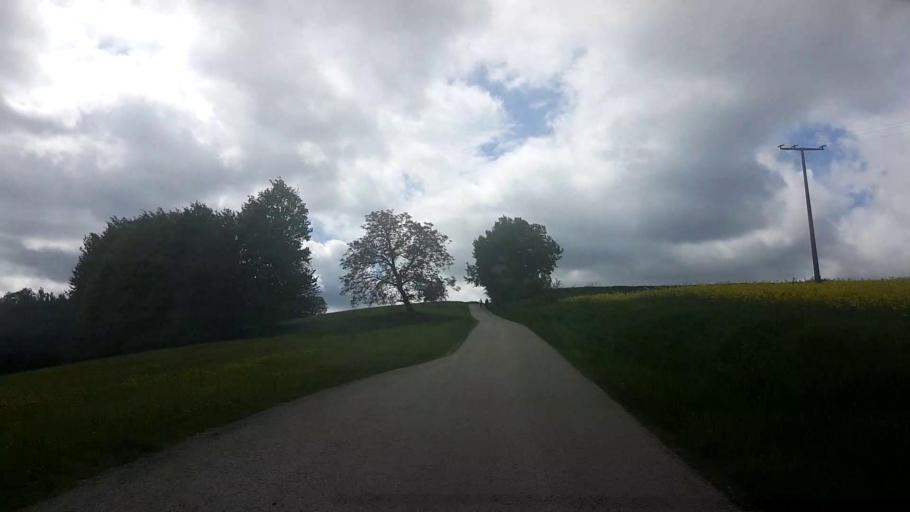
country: DE
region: Bavaria
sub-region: Upper Franconia
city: Bad Staffelstein
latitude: 50.1067
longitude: 11.0371
